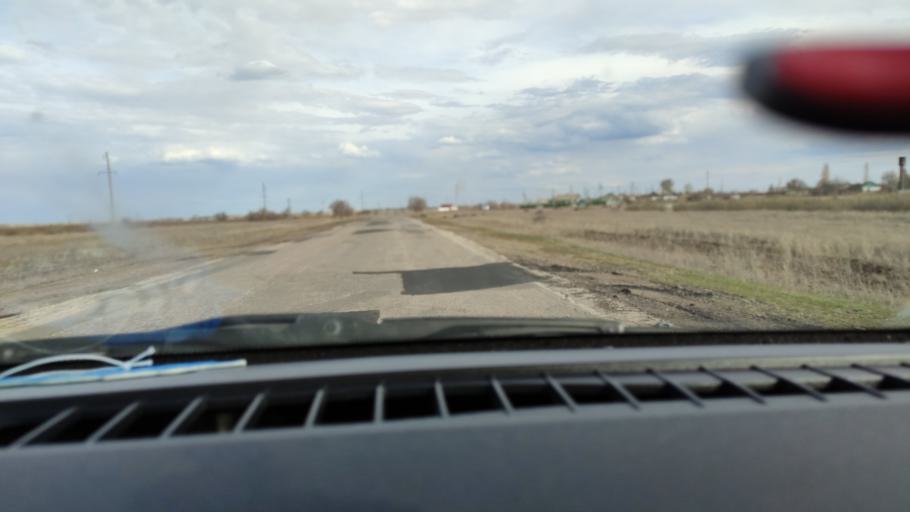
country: RU
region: Saratov
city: Rovnoye
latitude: 51.0611
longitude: 46.0215
